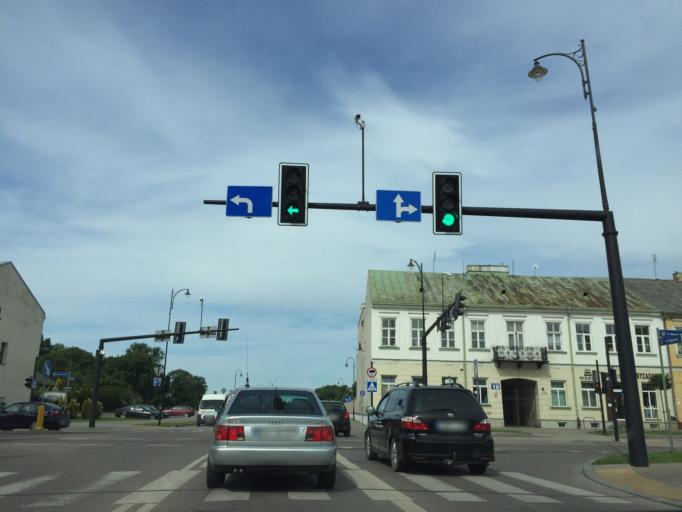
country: PL
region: Podlasie
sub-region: Suwalki
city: Suwalki
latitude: 54.0954
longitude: 22.9292
